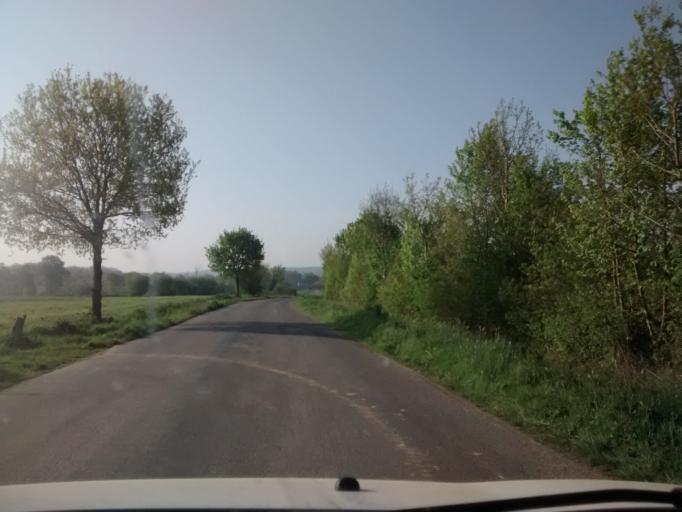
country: FR
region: Brittany
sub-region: Departement d'Ille-et-Vilaine
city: Saint-Jean-sur-Couesnon
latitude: 48.2827
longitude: -1.3793
